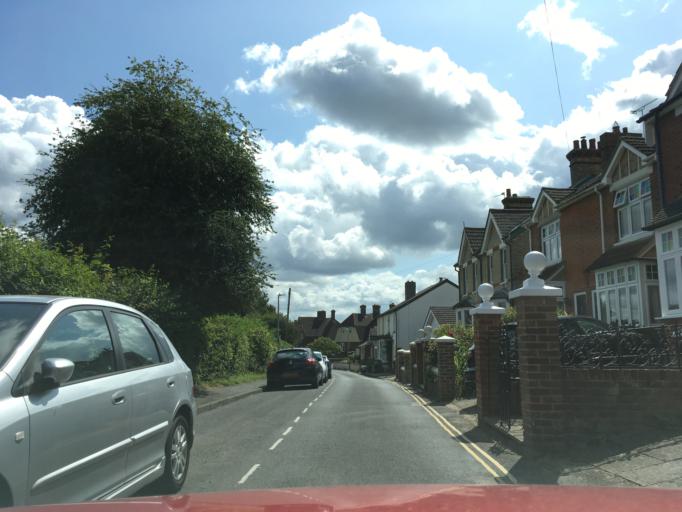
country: GB
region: England
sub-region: Kent
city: West Malling
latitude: 51.2957
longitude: 0.4019
